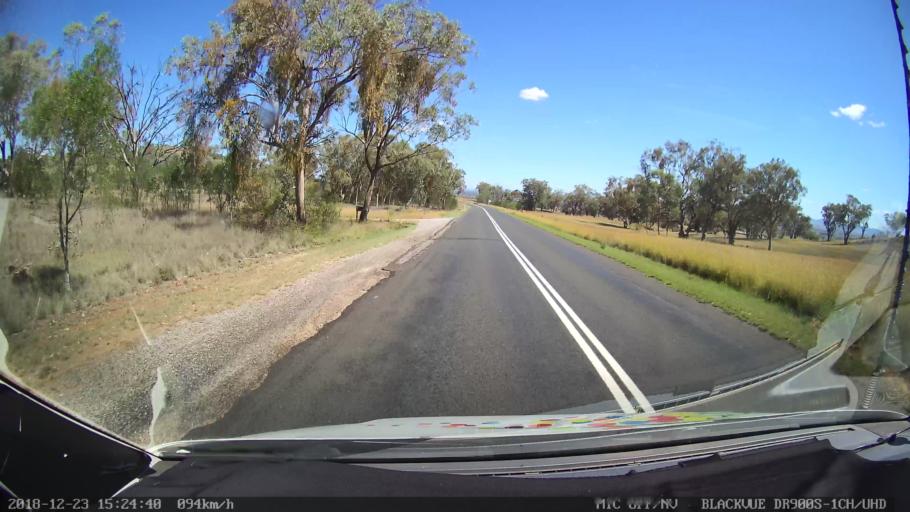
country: AU
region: New South Wales
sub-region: Tamworth Municipality
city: Manilla
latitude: -30.8946
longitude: 150.8245
